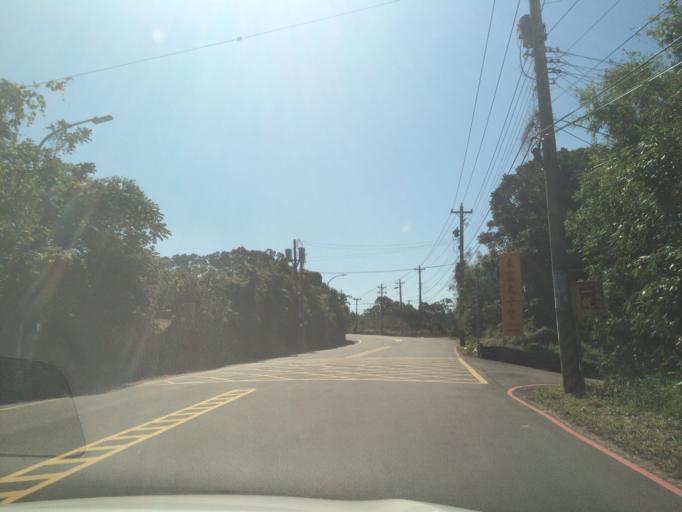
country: TW
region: Taiwan
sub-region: Hsinchu
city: Hsinchu
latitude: 24.7668
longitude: 120.9634
